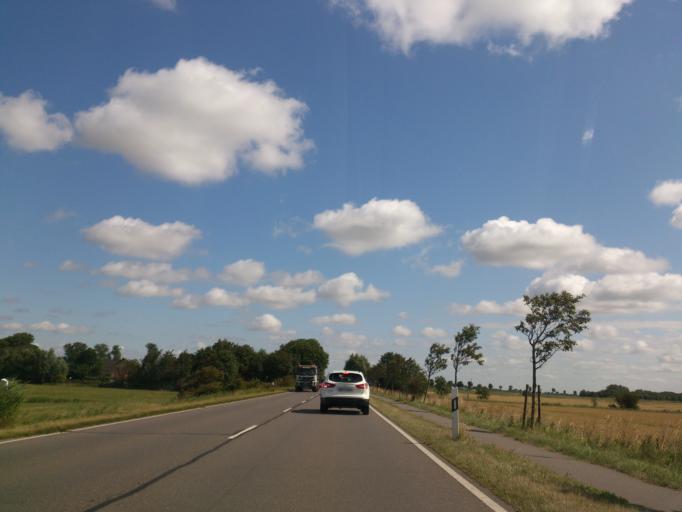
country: DE
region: Schleswig-Holstein
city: Tating
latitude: 54.3041
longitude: 8.7200
